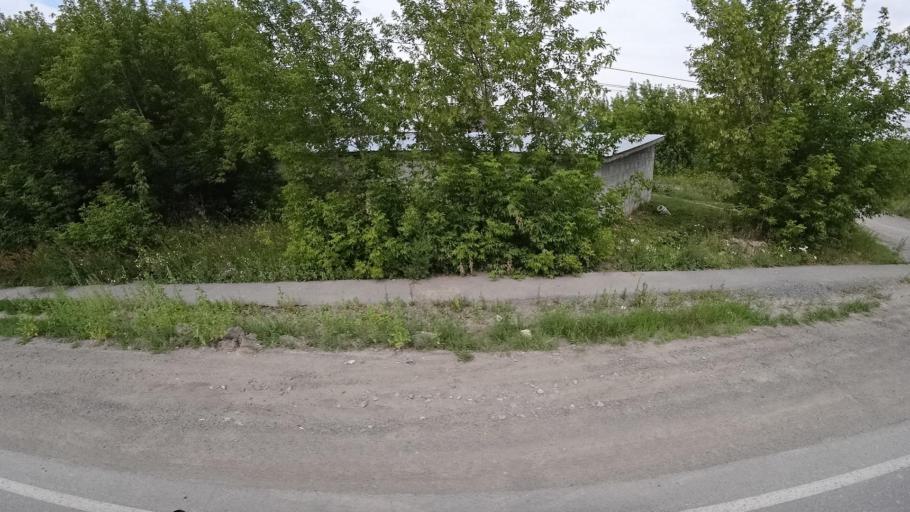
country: RU
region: Sverdlovsk
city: Kamyshlov
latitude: 56.8545
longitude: 62.7188
